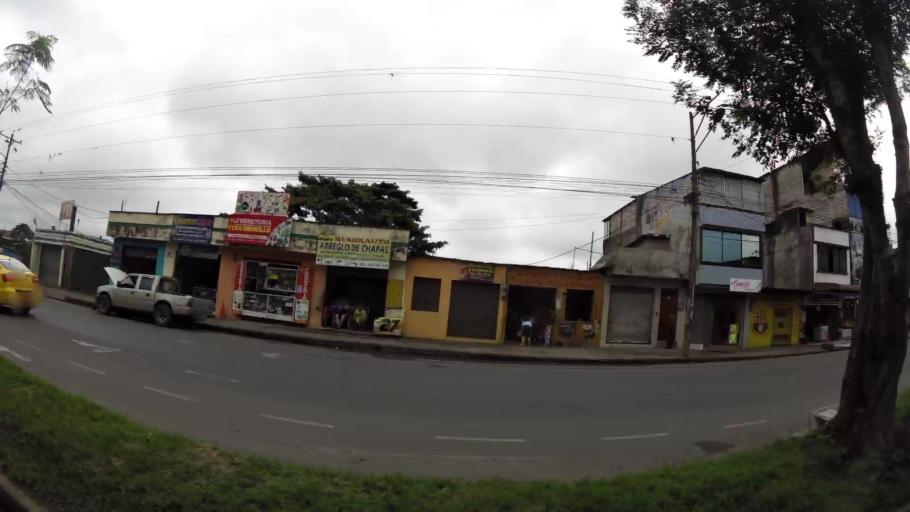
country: EC
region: Santo Domingo de los Tsachilas
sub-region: Canton Santo Domingo de los Colorados
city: Santo Domingo de los Colorados
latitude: -0.2429
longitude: -79.1716
